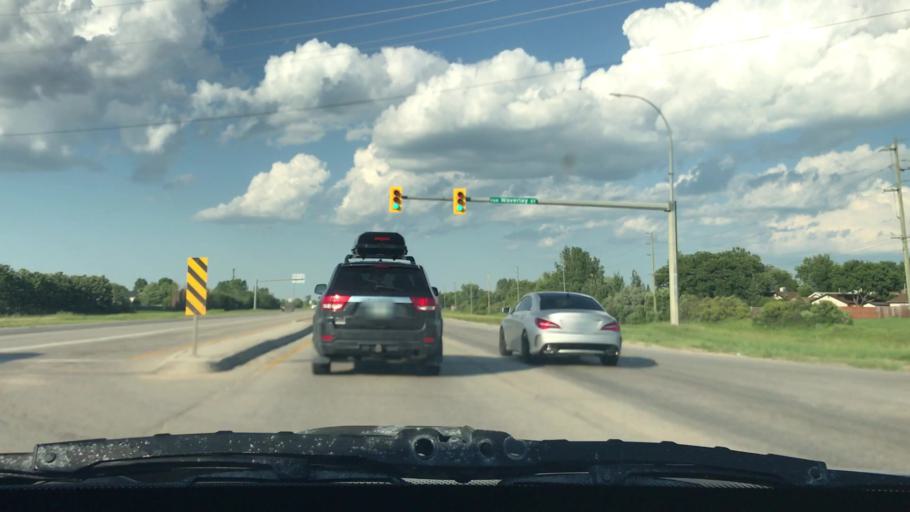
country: CA
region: Manitoba
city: Winnipeg
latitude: 49.7709
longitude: -97.1739
